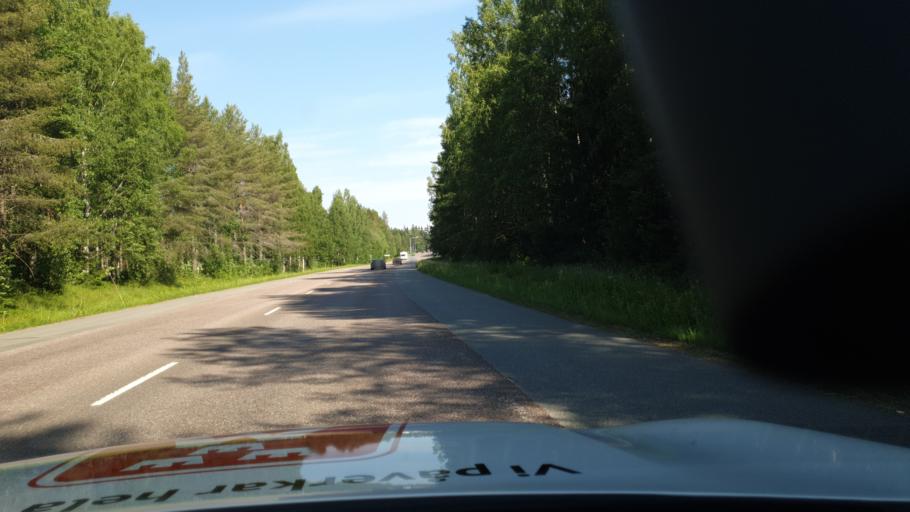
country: SE
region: Vaesterbotten
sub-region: Skelleftea Kommun
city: Skelleftea
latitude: 64.7582
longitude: 21.0087
